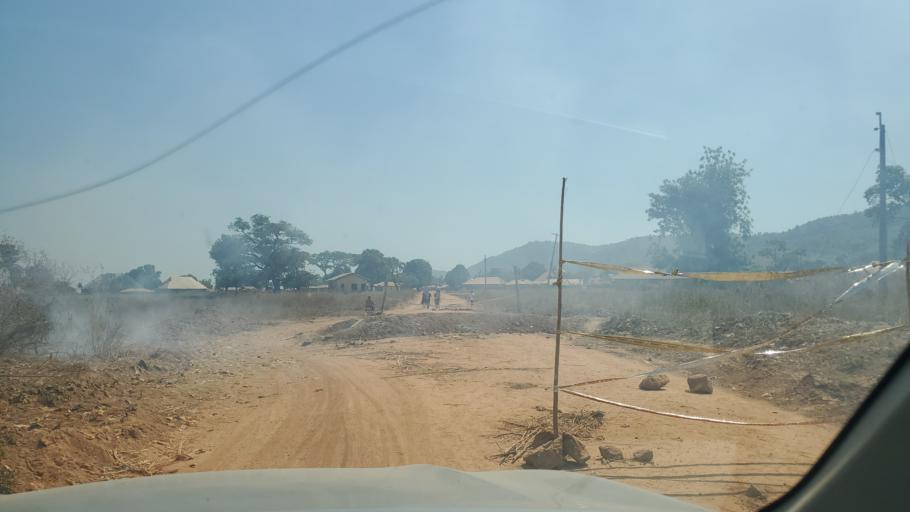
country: NG
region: Niger
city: Gawu Babangida
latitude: 9.2161
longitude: 6.8424
